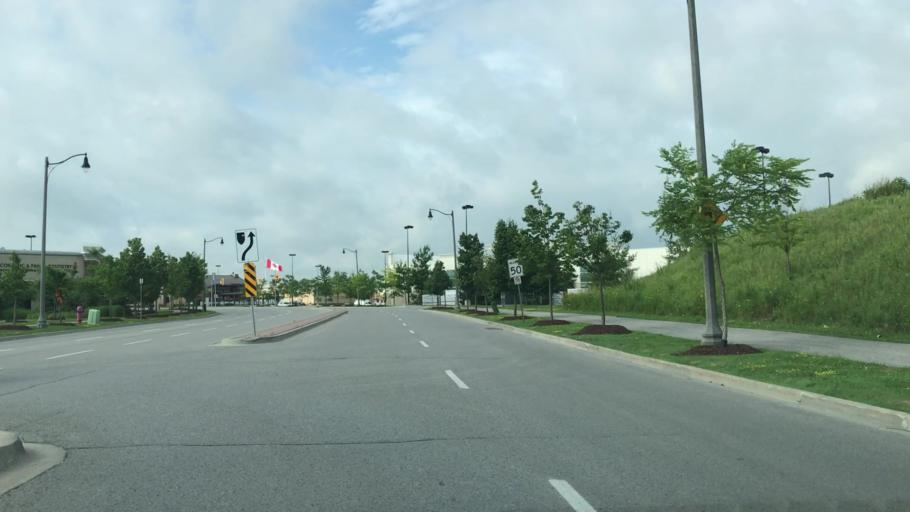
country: CA
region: Ontario
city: Newmarket
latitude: 44.0161
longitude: -79.4148
